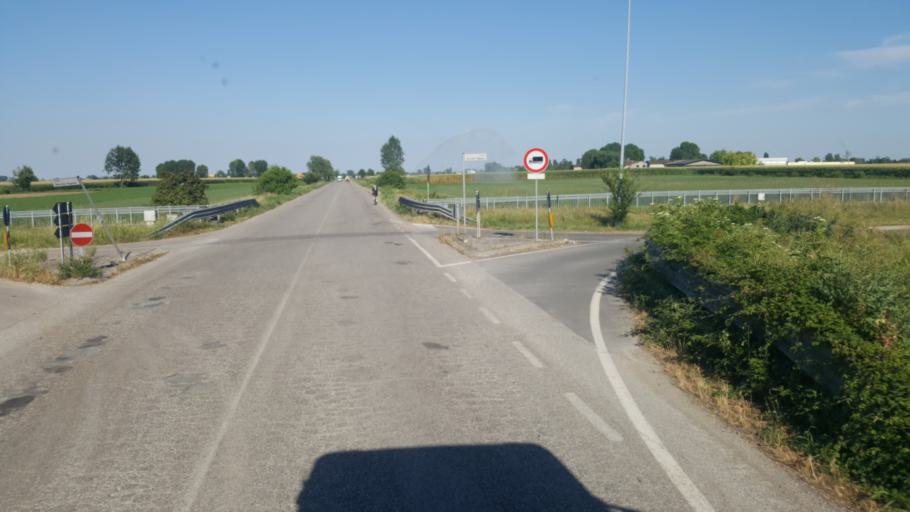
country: IT
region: Lombardy
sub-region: Provincia di Mantova
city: Asola
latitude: 45.2300
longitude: 10.4199
